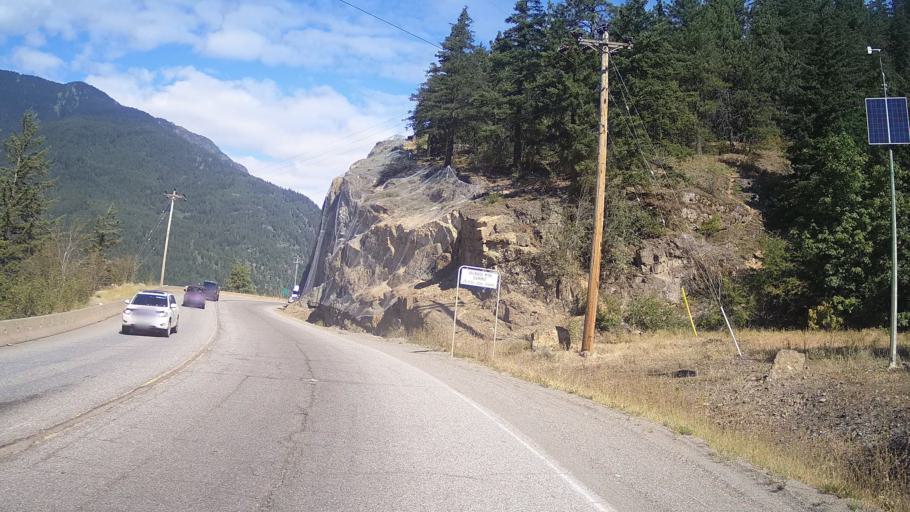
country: CA
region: British Columbia
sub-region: Thompson-Nicola Regional District
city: Ashcroft
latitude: 50.0758
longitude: -121.5479
